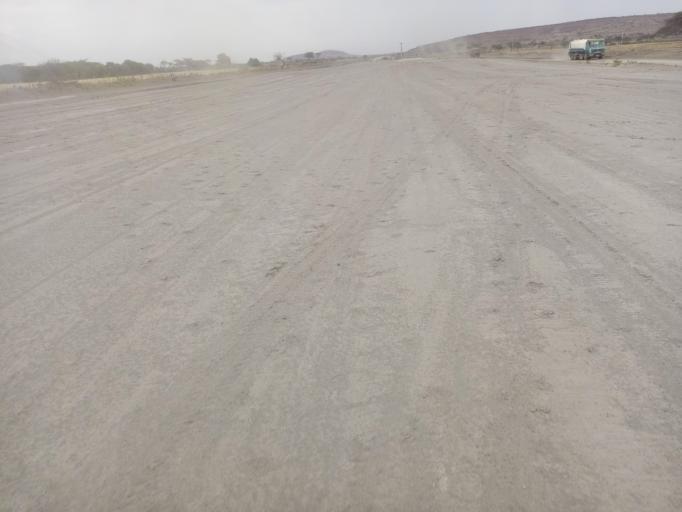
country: ET
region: Oromiya
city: Ziway
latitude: 7.8302
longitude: 38.6504
